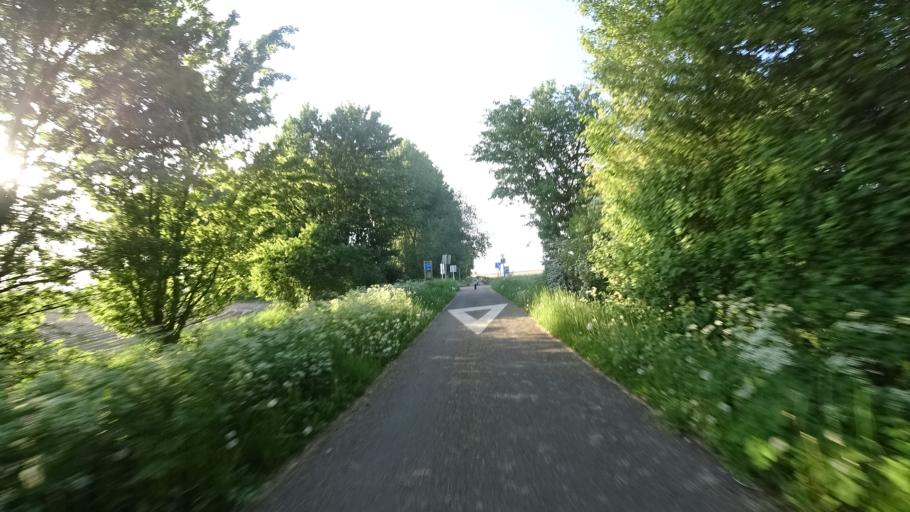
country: BE
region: Wallonia
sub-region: Province du Brabant Wallon
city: Ramillies
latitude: 50.6222
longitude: 4.9011
